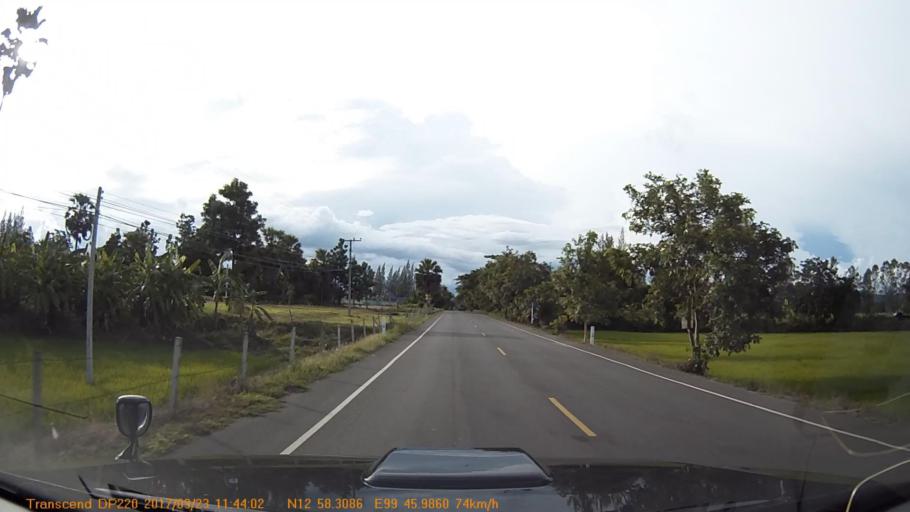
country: TH
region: Phetchaburi
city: Kaeng Krachan
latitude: 12.9720
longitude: 99.7663
